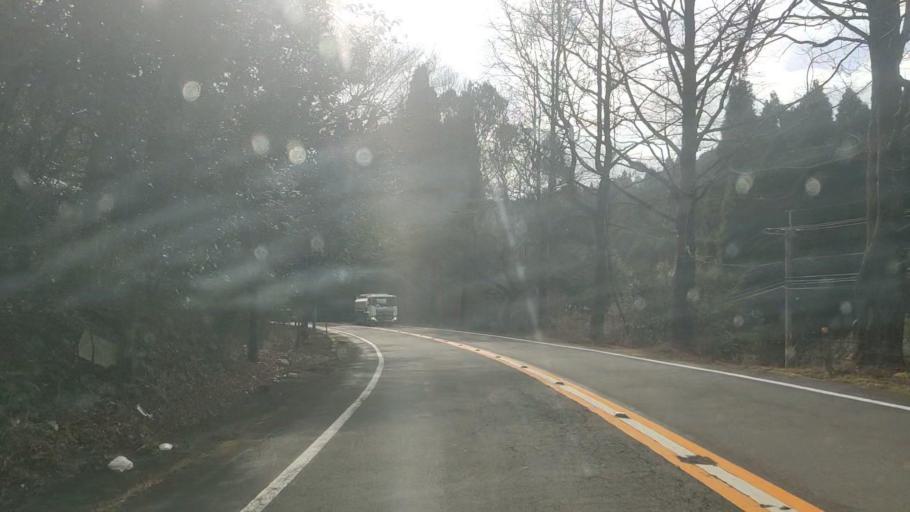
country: JP
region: Kumamoto
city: Hitoyoshi
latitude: 32.1075
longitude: 130.8047
